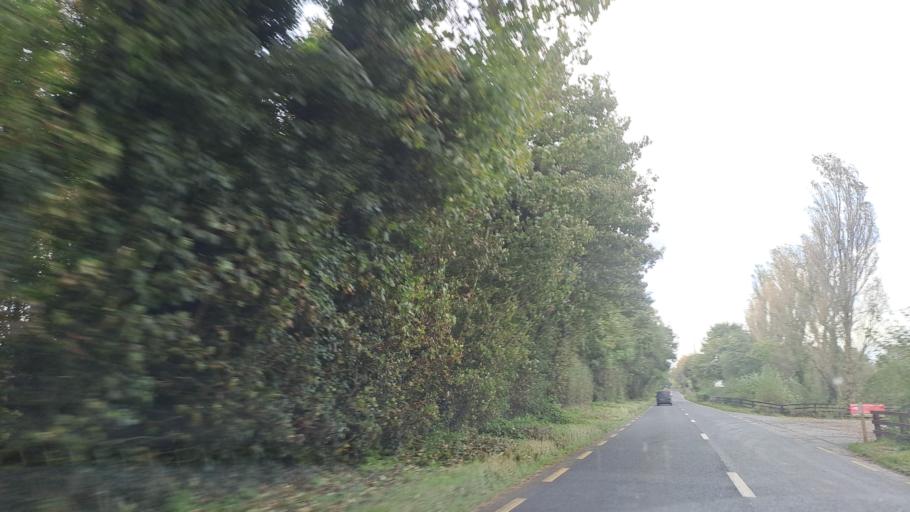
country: IE
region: Ulster
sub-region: An Cabhan
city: Kingscourt
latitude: 53.8647
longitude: -6.7935
